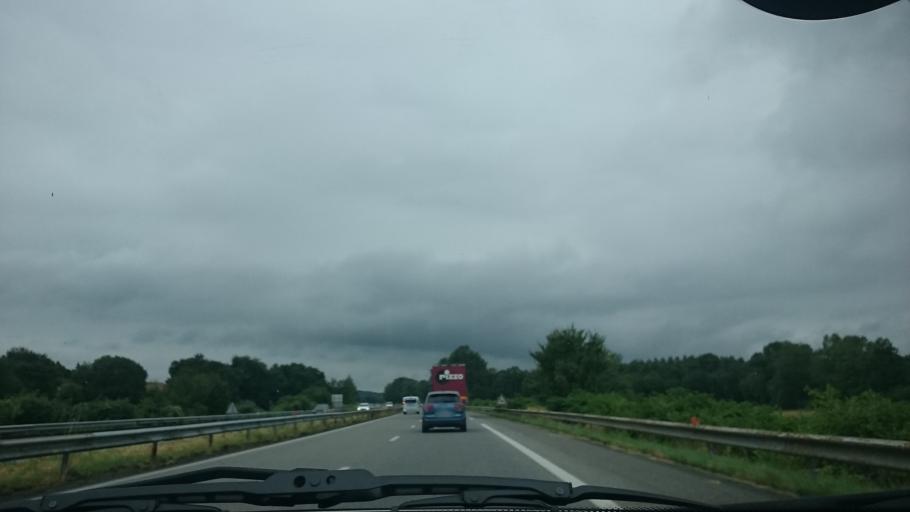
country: FR
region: Aquitaine
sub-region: Departement des Pyrenees-Atlantiques
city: Mont
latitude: 43.4573
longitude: -0.7046
